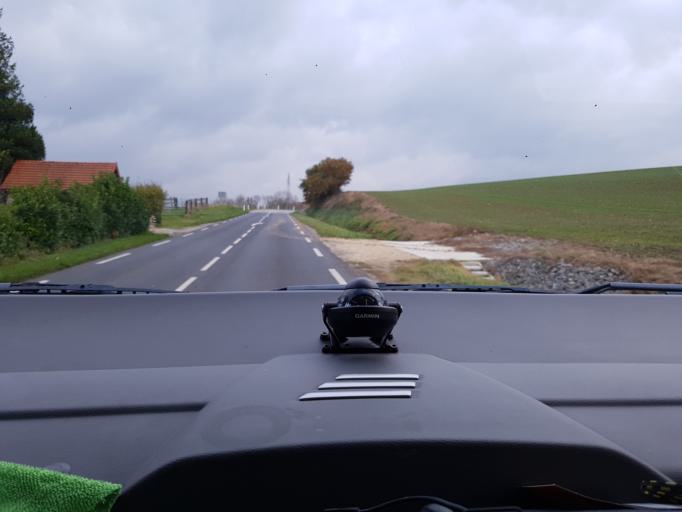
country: FR
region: Haute-Normandie
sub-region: Departement de la Seine-Maritime
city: Hautot-sur-Mer
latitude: 49.8970
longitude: 1.0515
